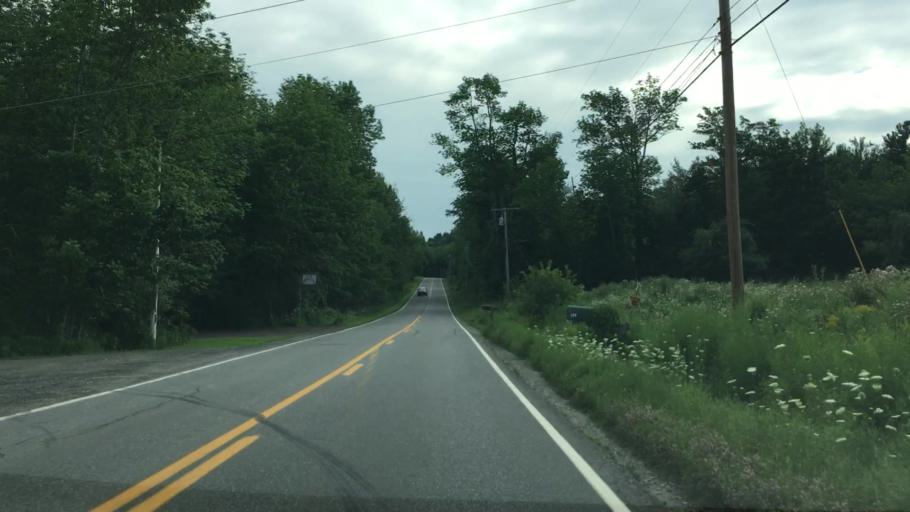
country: US
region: Maine
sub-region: Waldo County
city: Belfast
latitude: 44.3566
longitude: -69.0496
